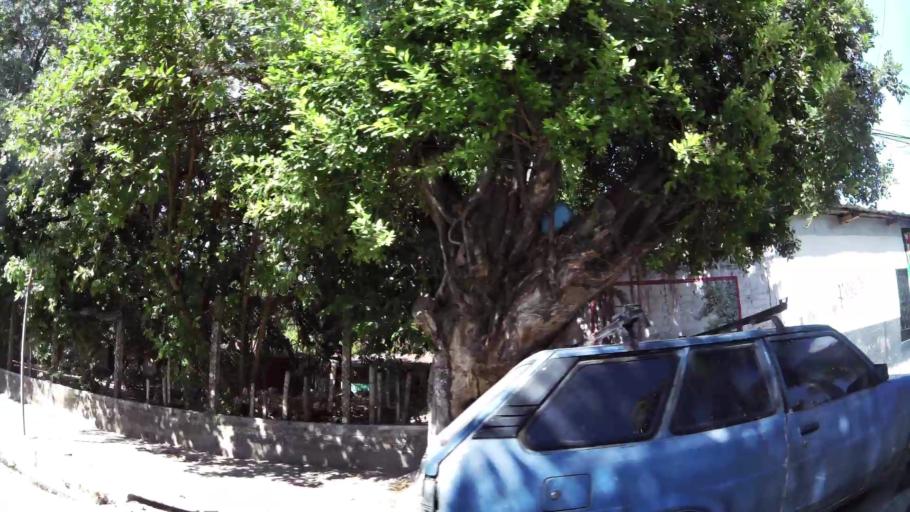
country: SV
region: San Salvador
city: Apopa
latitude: 13.8033
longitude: -89.1787
